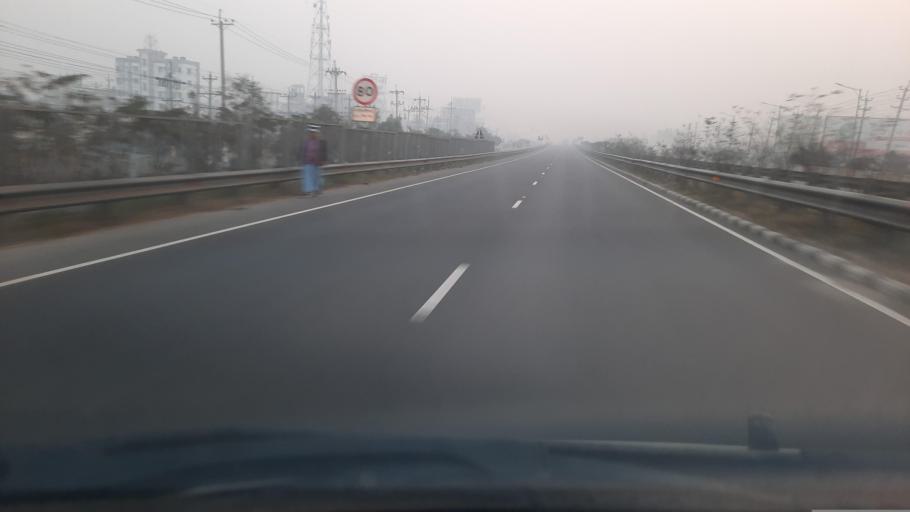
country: BD
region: Dhaka
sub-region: Dhaka
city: Dhaka
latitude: 23.6630
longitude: 90.3853
